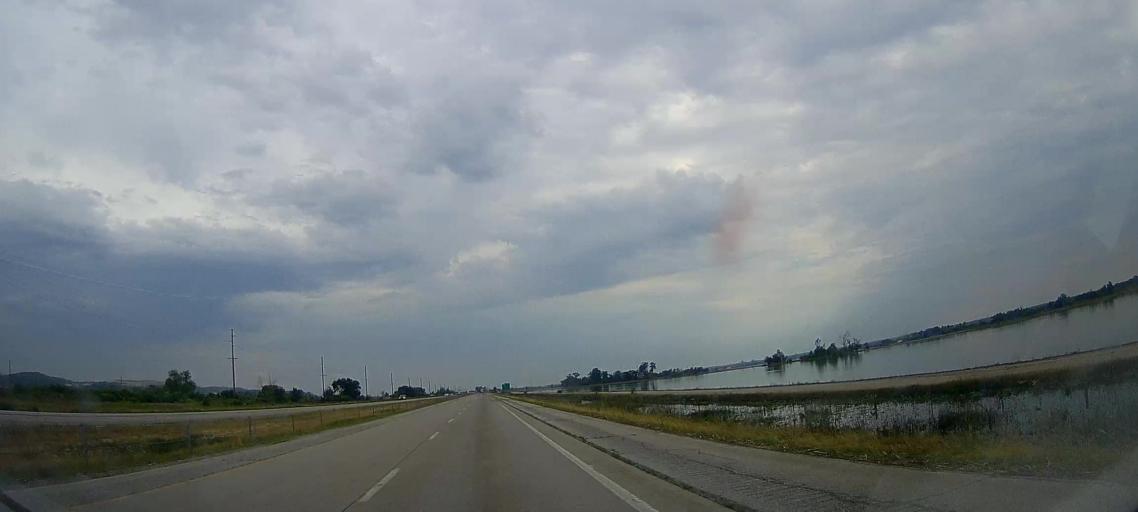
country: US
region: Iowa
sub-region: Pottawattamie County
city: Carter Lake
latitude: 41.3785
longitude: -95.8997
